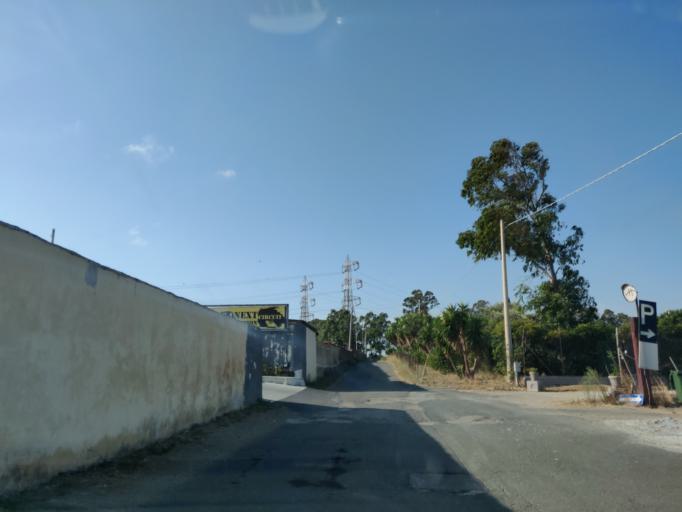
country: IT
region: Latium
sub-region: Citta metropolitana di Roma Capitale
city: Aurelia
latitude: 42.1293
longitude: 11.7669
